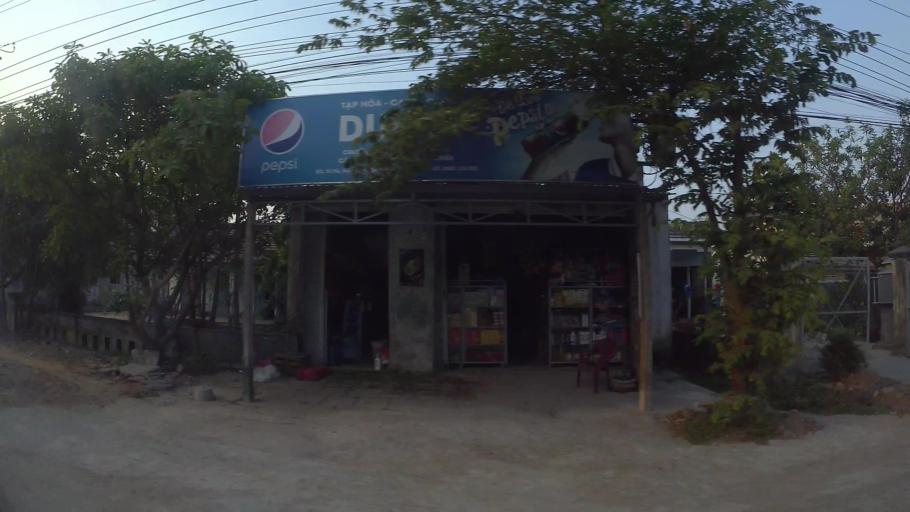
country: VN
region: Da Nang
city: Ngu Hanh Son
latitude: 15.9555
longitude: 108.2464
